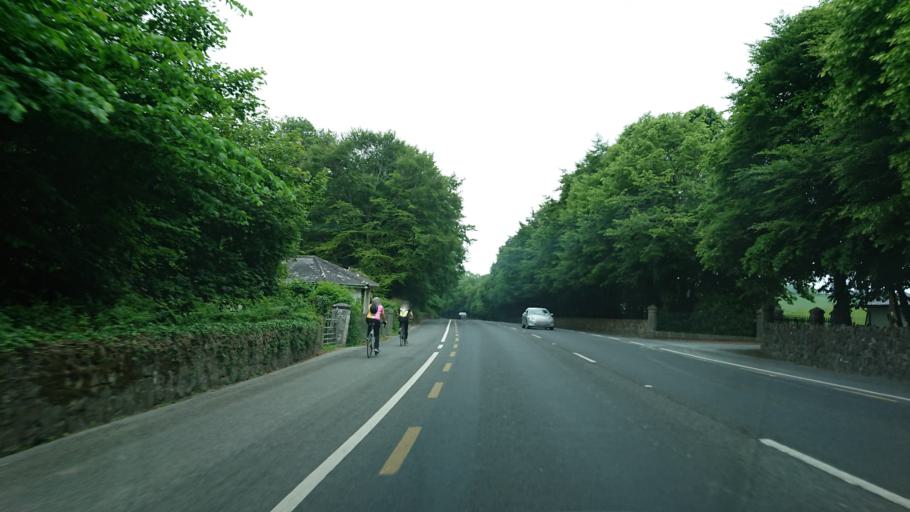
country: IE
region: Munster
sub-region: Waterford
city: Waterford
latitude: 52.2099
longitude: -7.1164
